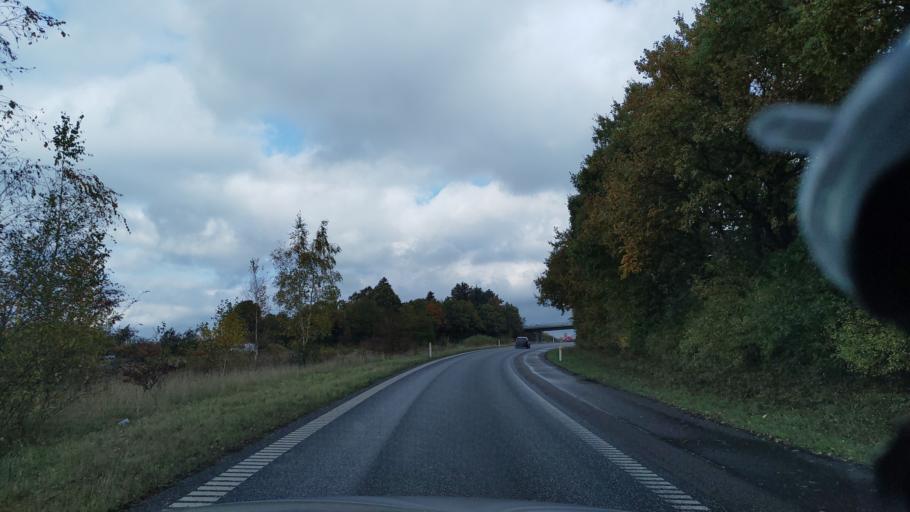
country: DK
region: Zealand
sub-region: Faxe Kommune
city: Ronnede
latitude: 55.2602
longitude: 11.9991
